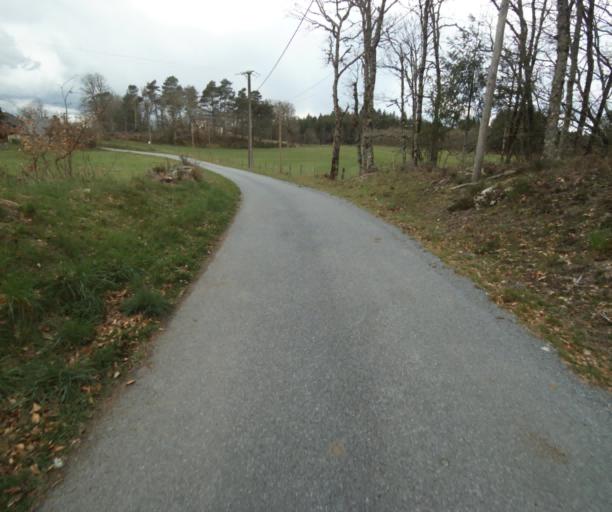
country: FR
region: Limousin
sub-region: Departement de la Correze
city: Correze
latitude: 45.2684
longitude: 1.9571
